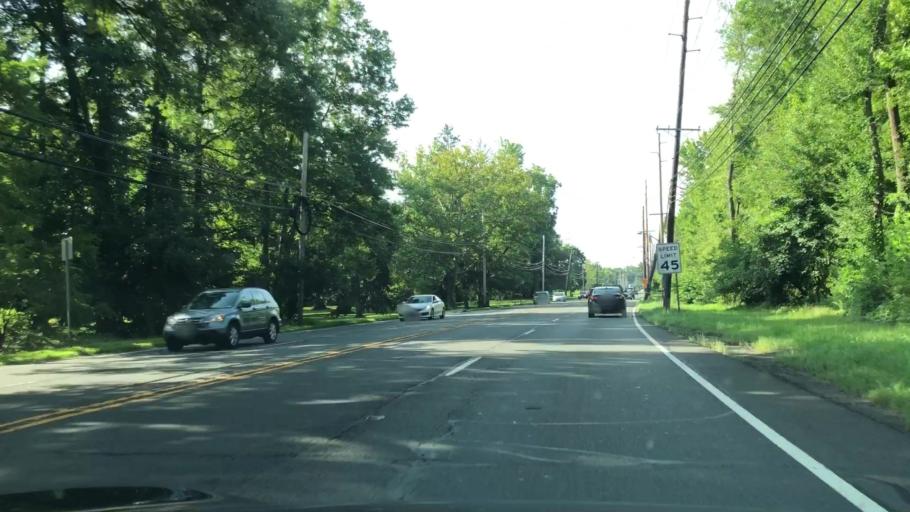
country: US
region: New Jersey
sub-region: Mercer County
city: Pennington
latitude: 40.3051
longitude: -74.7847
